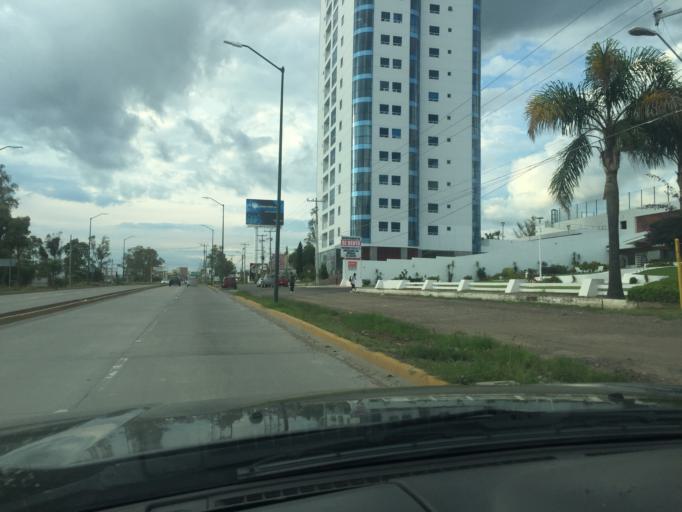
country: MX
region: Guanajuato
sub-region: Leon
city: La Ermita
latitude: 21.1582
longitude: -101.7223
